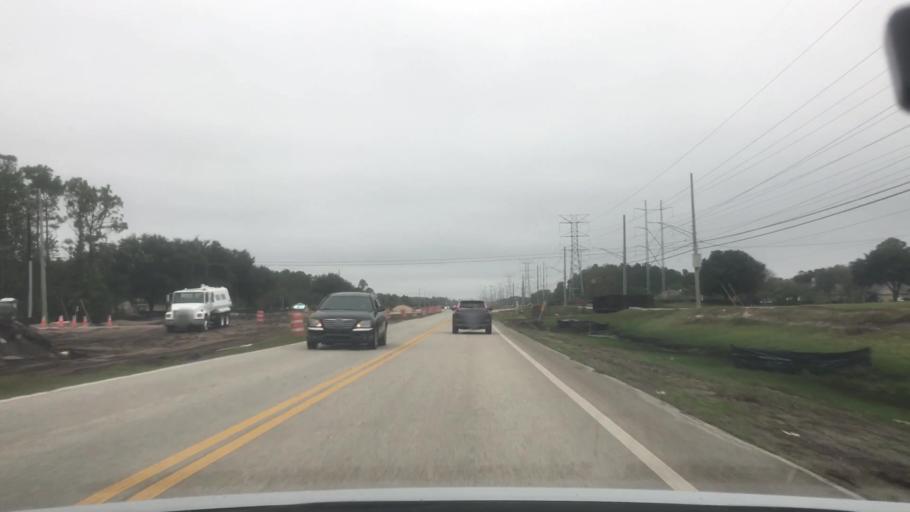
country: US
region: Florida
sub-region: Duval County
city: Atlantic Beach
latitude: 30.3263
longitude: -81.4894
